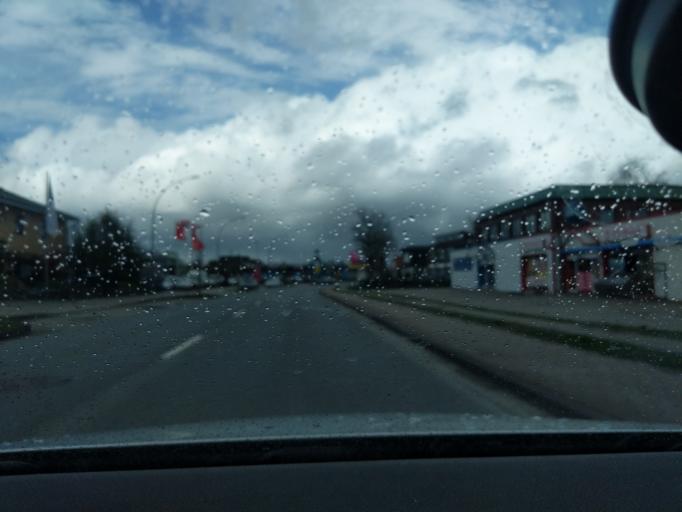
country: DE
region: Lower Saxony
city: Stade
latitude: 53.6079
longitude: 9.4770
